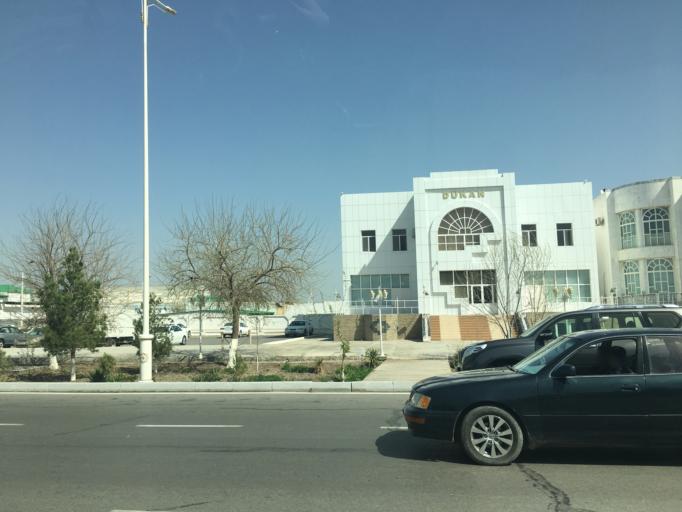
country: TM
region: Lebap
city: Turkmenabat
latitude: 39.0652
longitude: 63.5873
